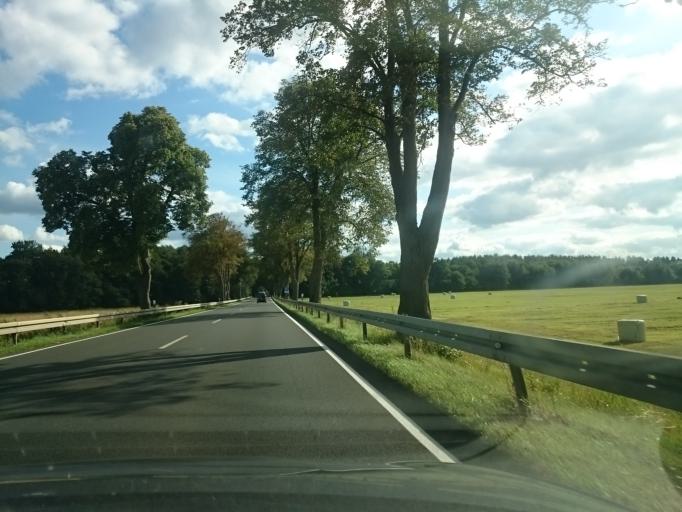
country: DE
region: Mecklenburg-Vorpommern
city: Neustrelitz
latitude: 53.3173
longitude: 13.0991
